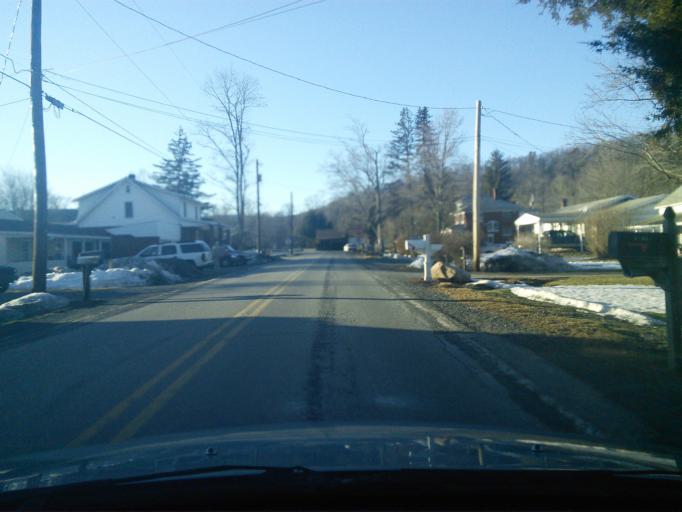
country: US
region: Pennsylvania
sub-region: Centre County
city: Park Forest Village
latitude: 40.8634
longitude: -77.9379
